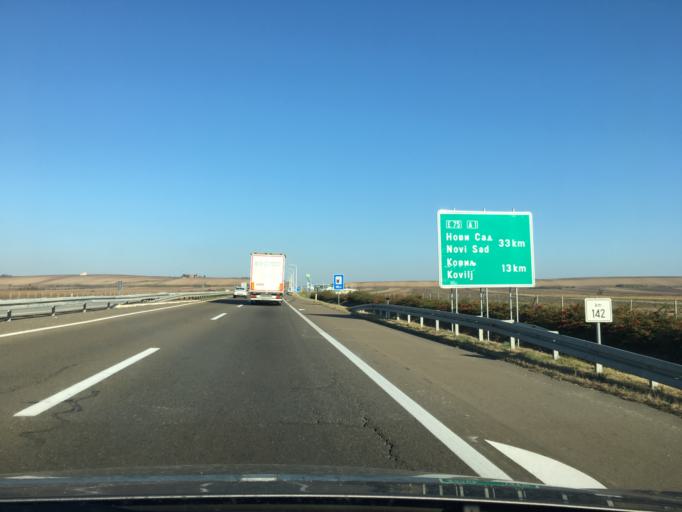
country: RS
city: Beska
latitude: 45.1414
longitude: 20.0856
